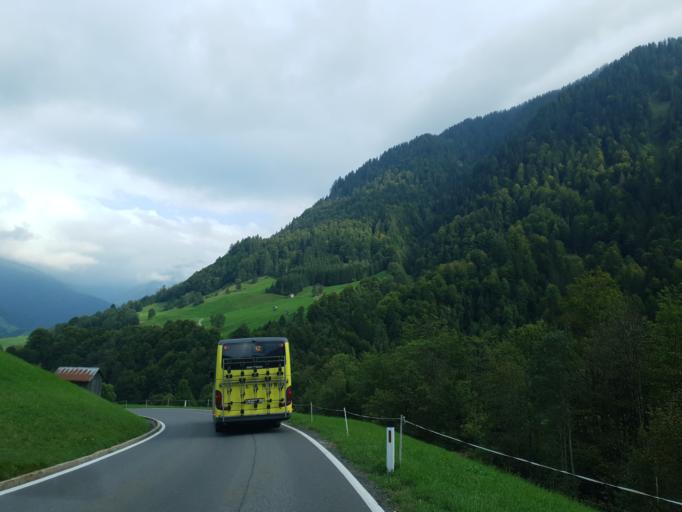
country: AT
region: Vorarlberg
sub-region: Politischer Bezirk Bregenz
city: Au
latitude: 47.3163
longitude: 9.9552
